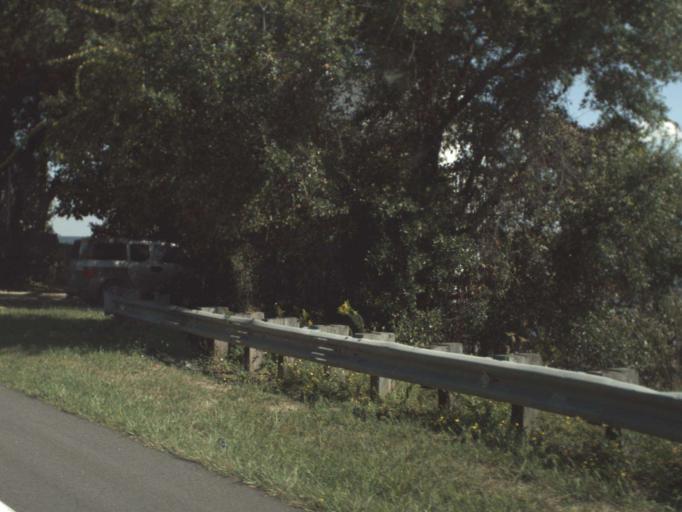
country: US
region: Florida
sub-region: Walton County
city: Miramar Beach
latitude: 30.4656
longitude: -86.3580
